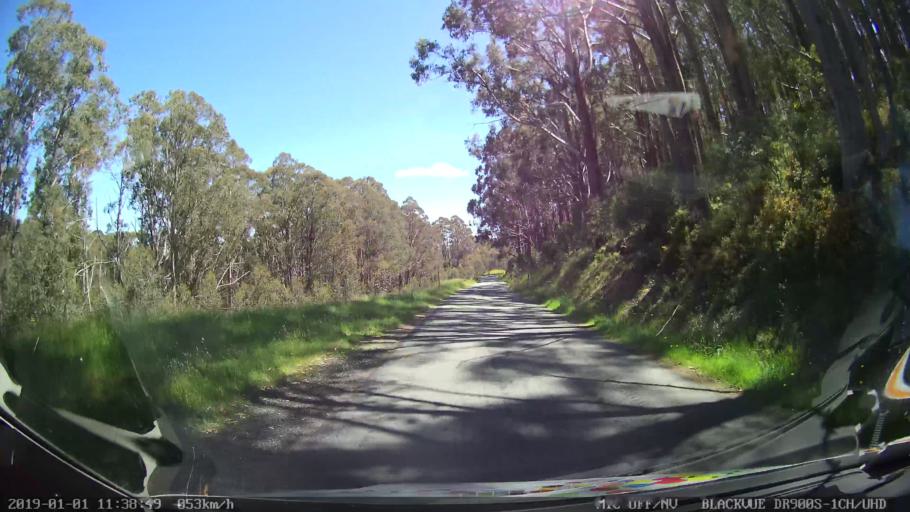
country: AU
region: New South Wales
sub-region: Snowy River
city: Jindabyne
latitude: -35.9316
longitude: 148.3866
